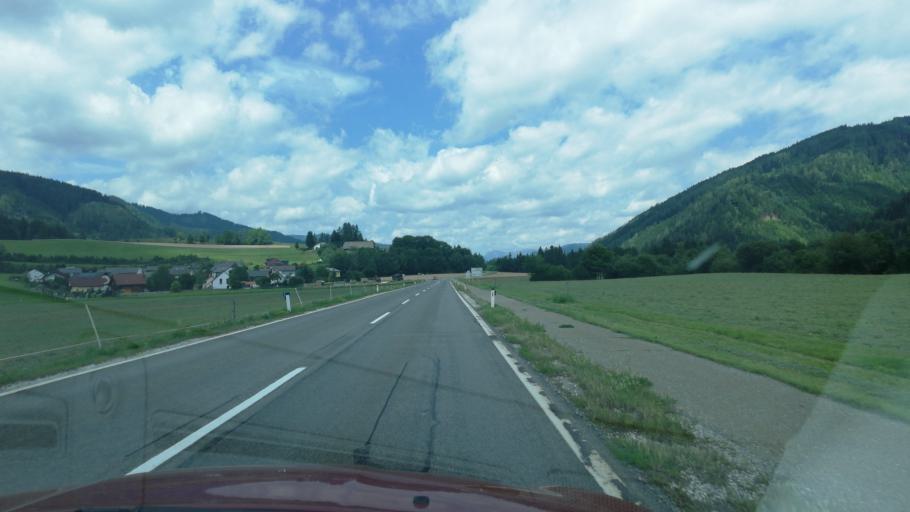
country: AT
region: Styria
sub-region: Politischer Bezirk Murtal
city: Oberkurzheim
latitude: 47.2305
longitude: 14.5520
